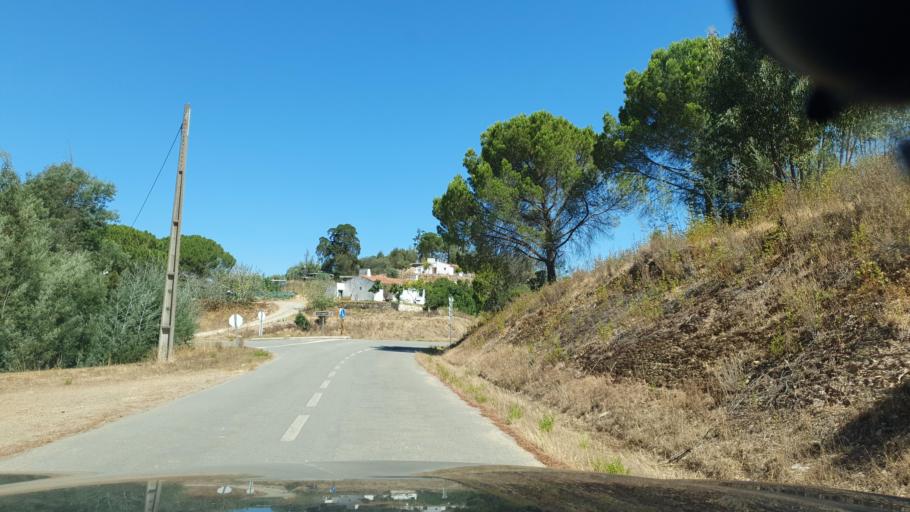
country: PT
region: Beja
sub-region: Odemira
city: Odemira
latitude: 37.5070
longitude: -8.4366
